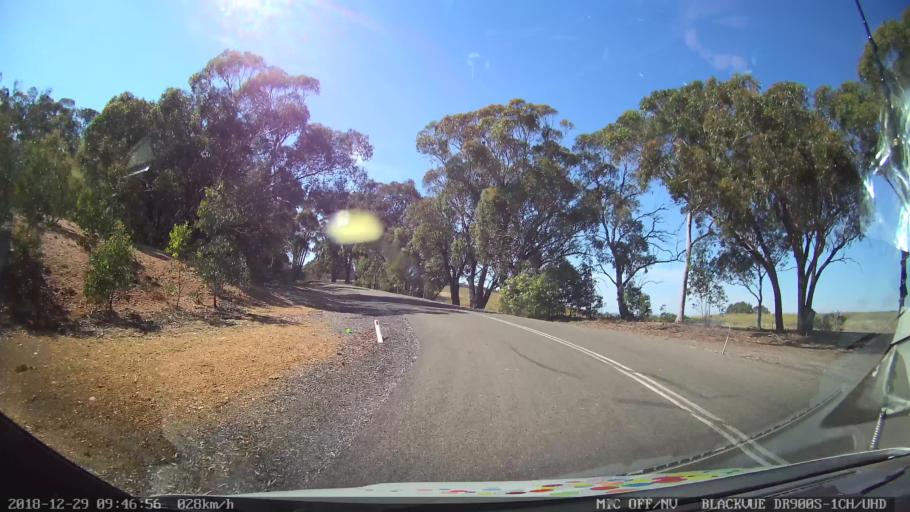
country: AU
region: New South Wales
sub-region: Upper Lachlan Shire
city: Crookwell
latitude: -34.7039
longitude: 149.4479
